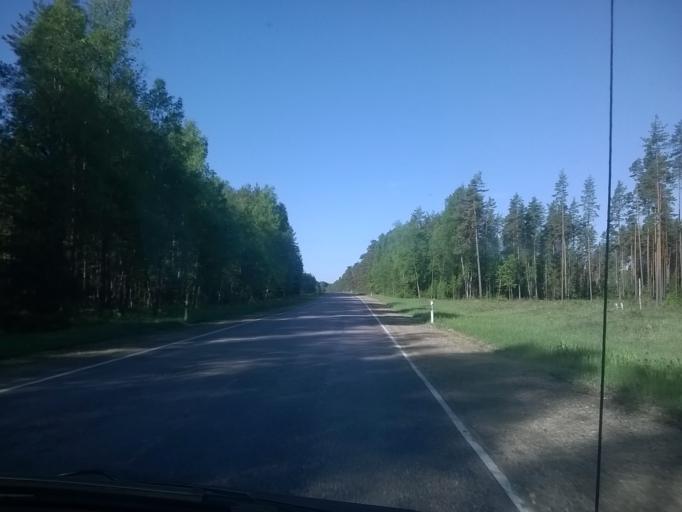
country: LV
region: Strenci
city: Seda
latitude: 57.6296
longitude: 25.8062
